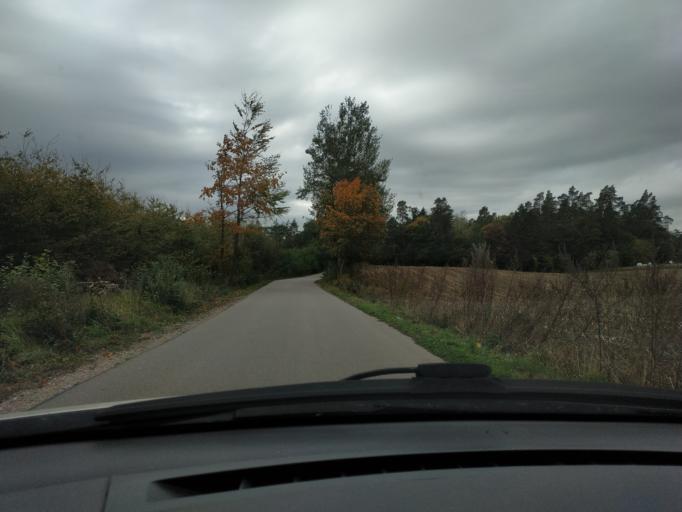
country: PL
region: Warmian-Masurian Voivodeship
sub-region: Powiat nowomiejski
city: Biskupiec
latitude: 53.4521
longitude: 19.3122
